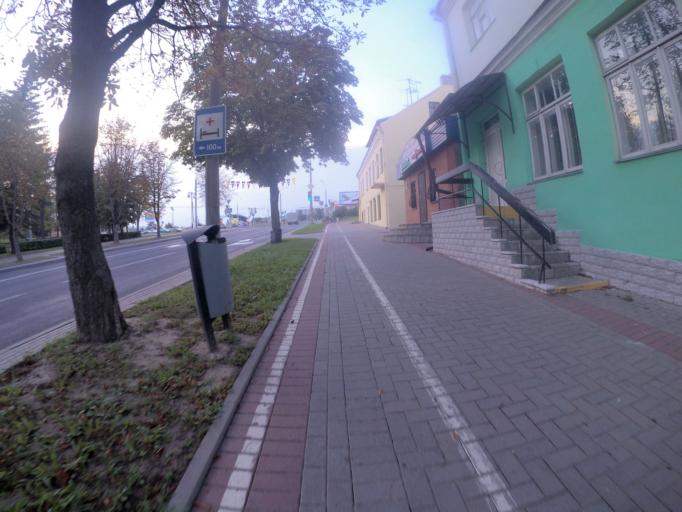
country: BY
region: Grodnenskaya
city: Hrodna
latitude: 53.6882
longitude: 23.8281
